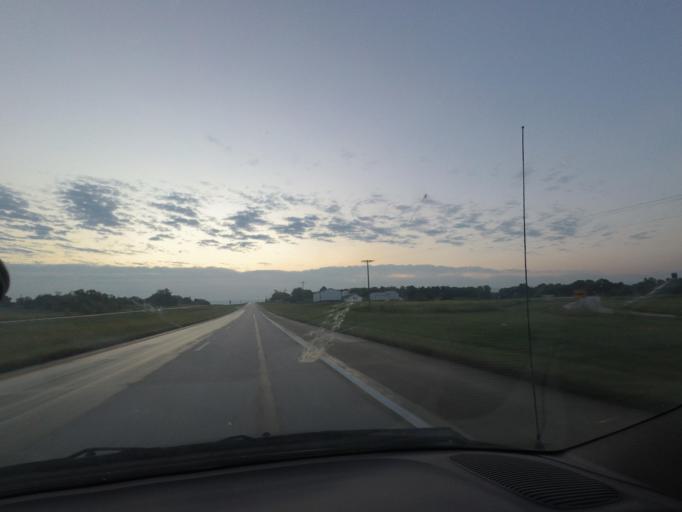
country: US
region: Missouri
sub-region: Macon County
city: Macon
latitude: 39.7594
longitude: -92.6716
